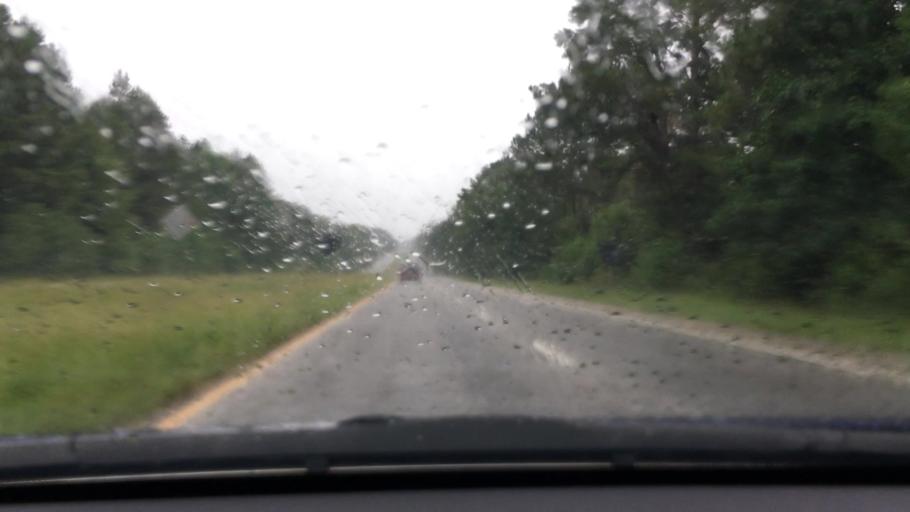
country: US
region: South Carolina
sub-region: Sumter County
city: Stateburg
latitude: 33.9499
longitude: -80.5522
